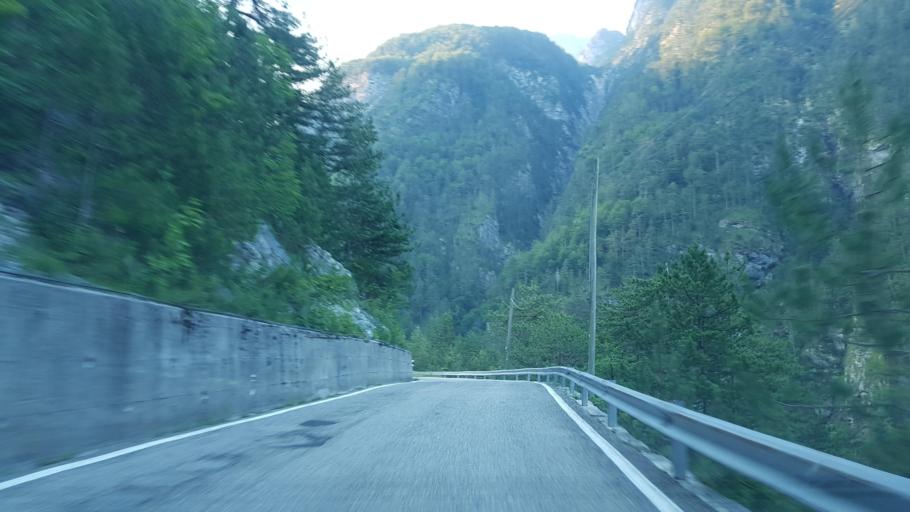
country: IT
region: Friuli Venezia Giulia
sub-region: Provincia di Udine
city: Dogna
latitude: 46.4481
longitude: 13.3526
